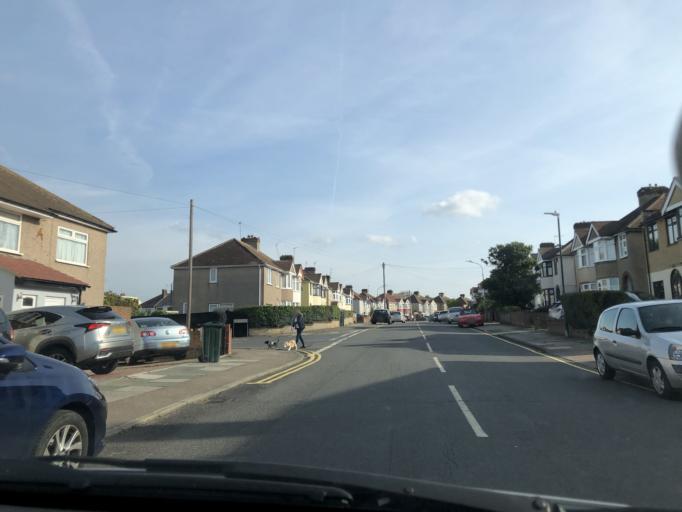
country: GB
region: England
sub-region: Greater London
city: Bexley
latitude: 51.4444
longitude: 0.1839
